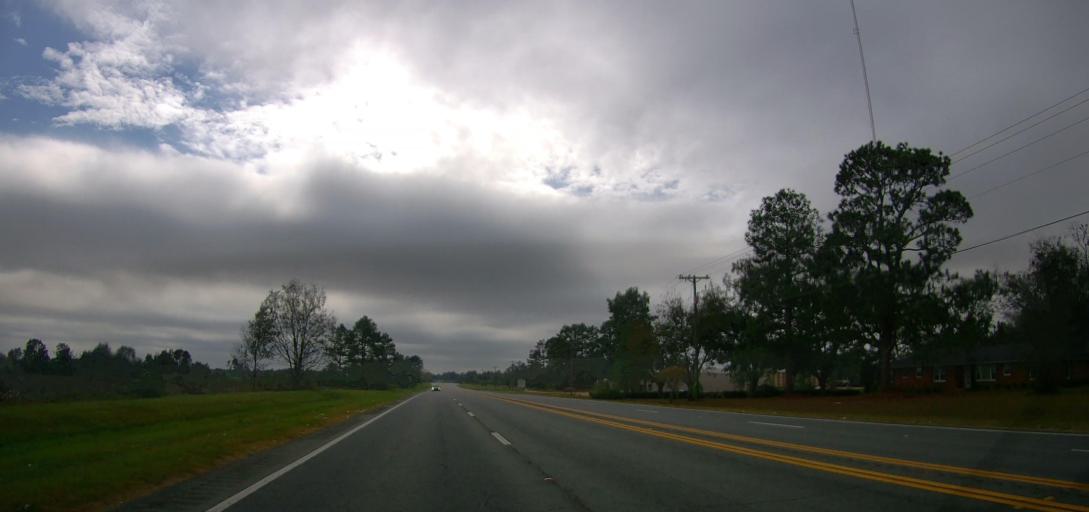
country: US
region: Georgia
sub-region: Tift County
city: Omega
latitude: 31.3599
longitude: -83.5787
